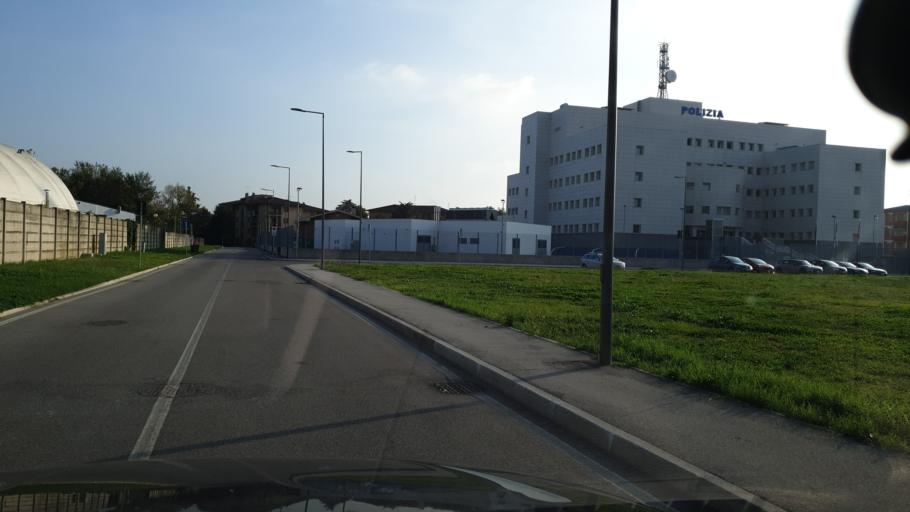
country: IT
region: Veneto
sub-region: Provincia di Rovigo
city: Rovigo
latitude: 45.0749
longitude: 11.8028
